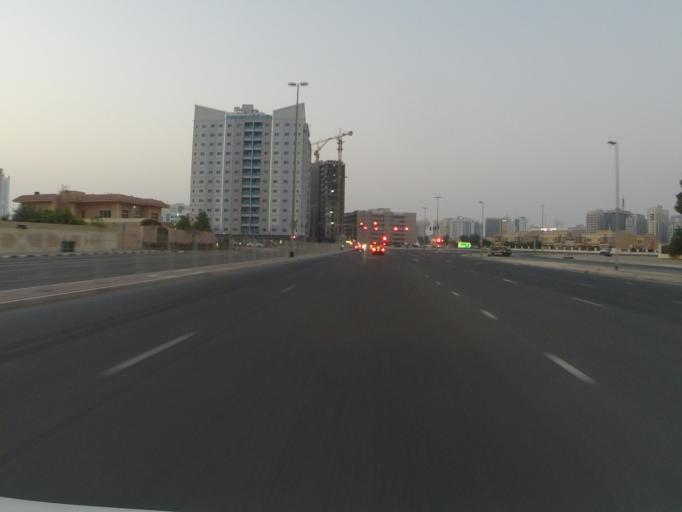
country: AE
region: Dubai
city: Dubai
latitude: 25.1046
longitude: 55.1994
